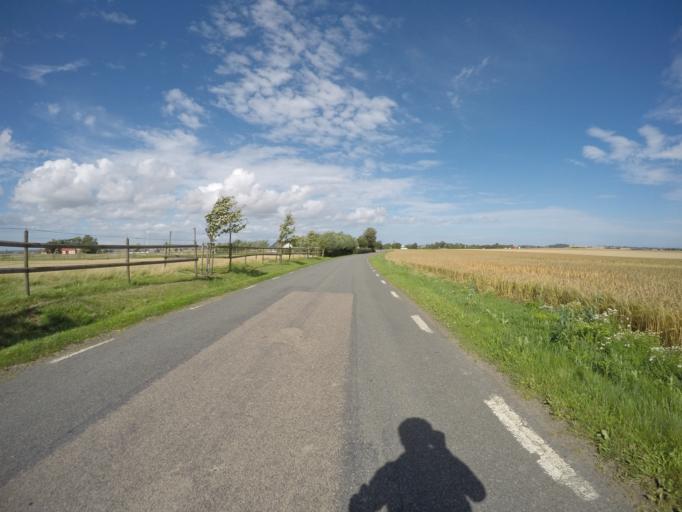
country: SE
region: Skane
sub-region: Simrishamns Kommun
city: Simrishamn
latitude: 55.4921
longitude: 14.1959
